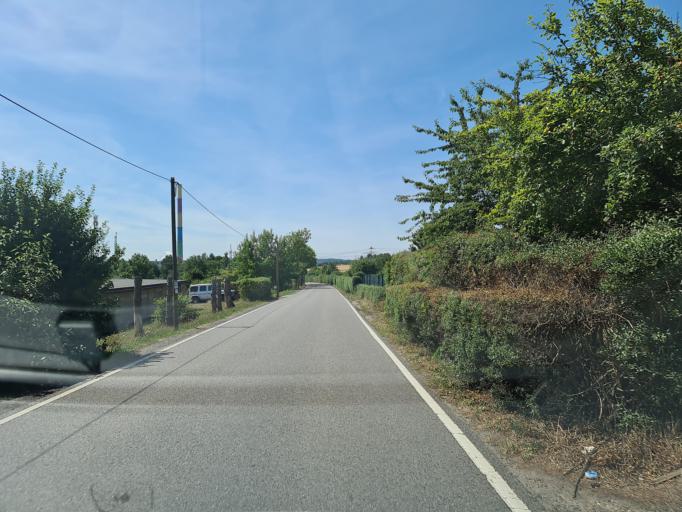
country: DE
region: Saxony
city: Hilbersdorf
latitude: 50.8651
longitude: 12.9452
